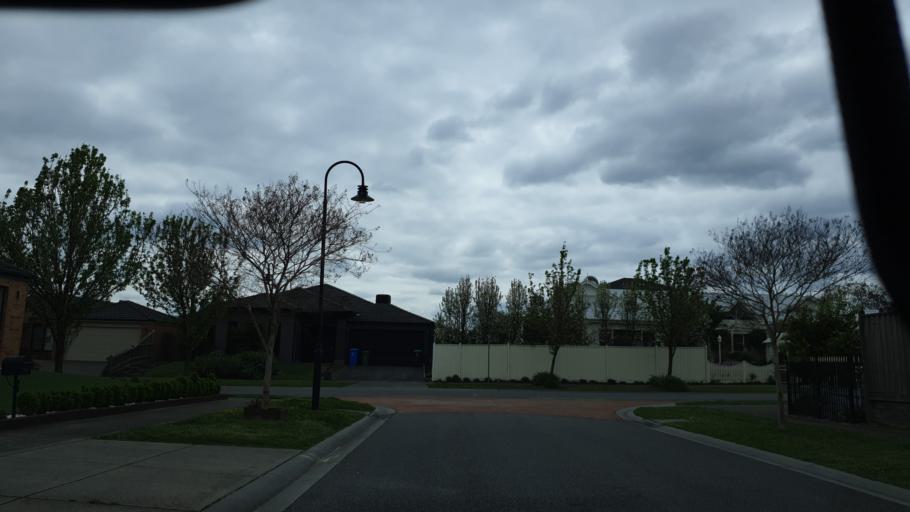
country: AU
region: Victoria
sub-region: Casey
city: Cranbourne North
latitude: -38.0735
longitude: 145.2896
